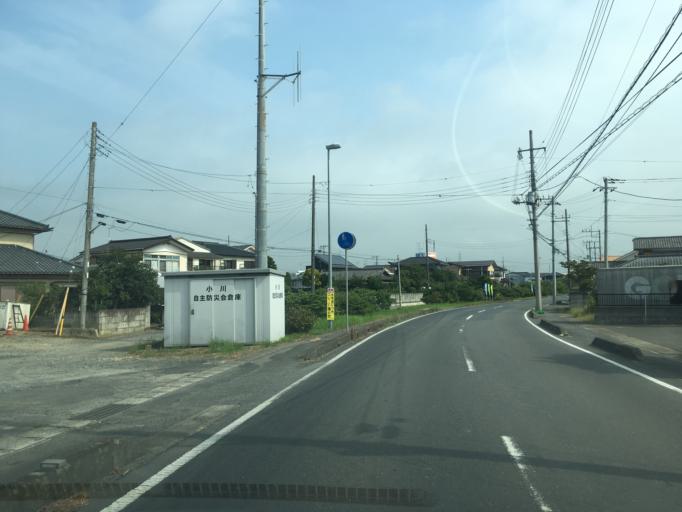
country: JP
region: Ibaraki
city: Oarai
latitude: 36.3421
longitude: 140.5820
